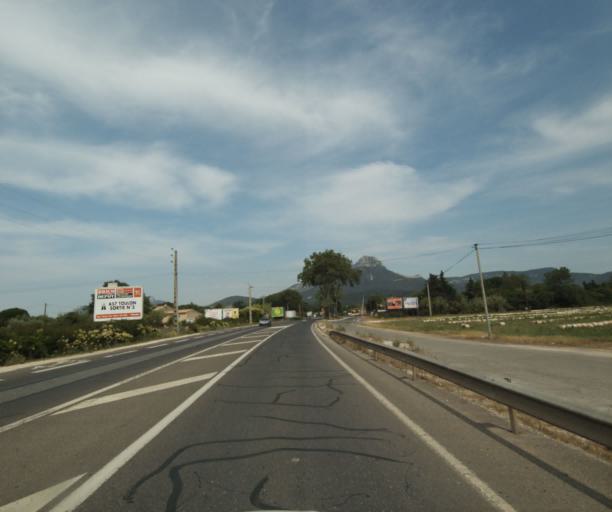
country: FR
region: Provence-Alpes-Cote d'Azur
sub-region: Departement du Var
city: La Crau
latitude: 43.1317
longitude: 6.0443
